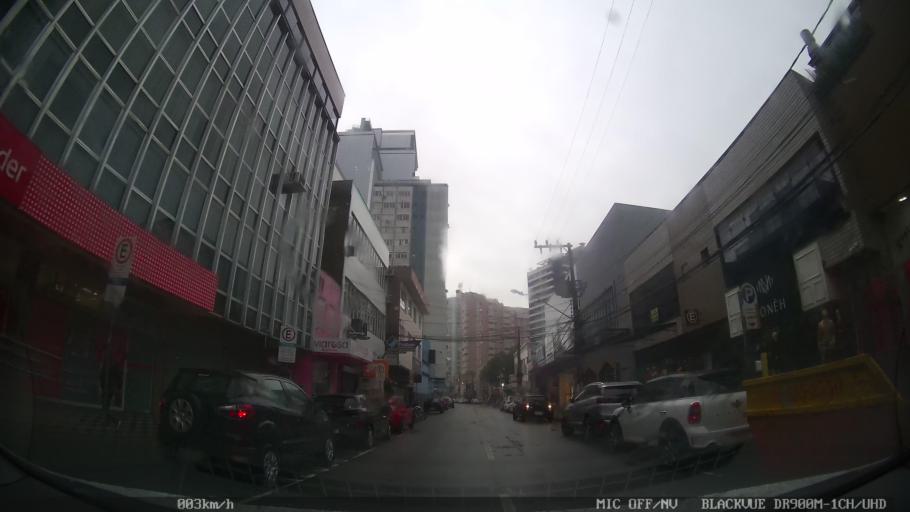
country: BR
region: Santa Catarina
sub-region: Itajai
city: Itajai
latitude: -26.9058
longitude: -48.6566
